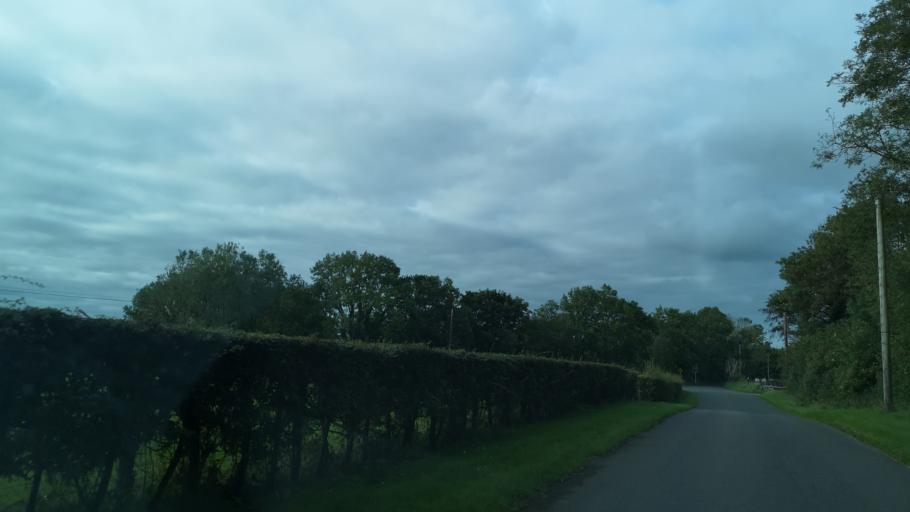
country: IE
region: Connaught
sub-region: County Galway
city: Ballinasloe
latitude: 53.3234
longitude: -8.1026
